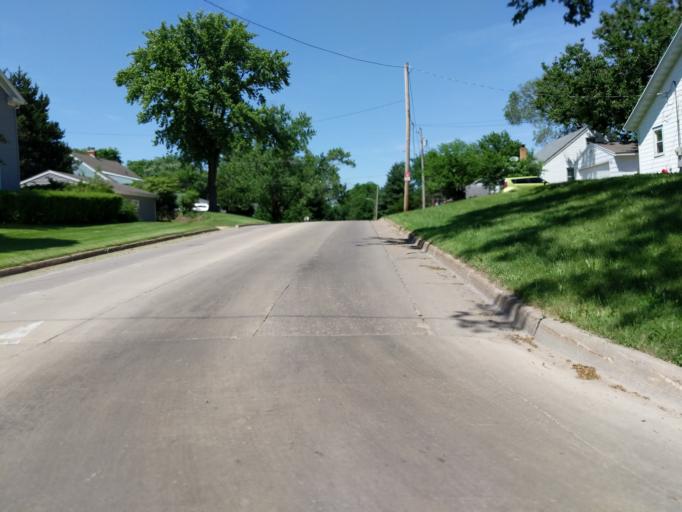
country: US
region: Iowa
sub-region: Linn County
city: Cedar Rapids
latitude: 42.0147
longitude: -91.6384
